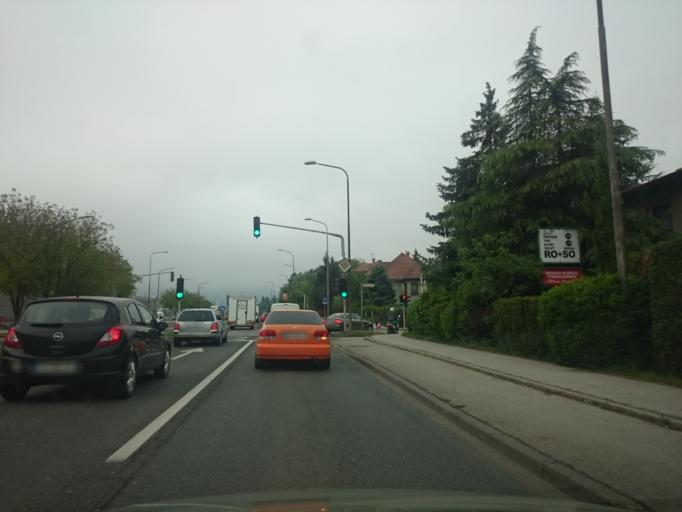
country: SI
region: Celje
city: Trnovlje pri Celju
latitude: 46.2510
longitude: 15.2802
